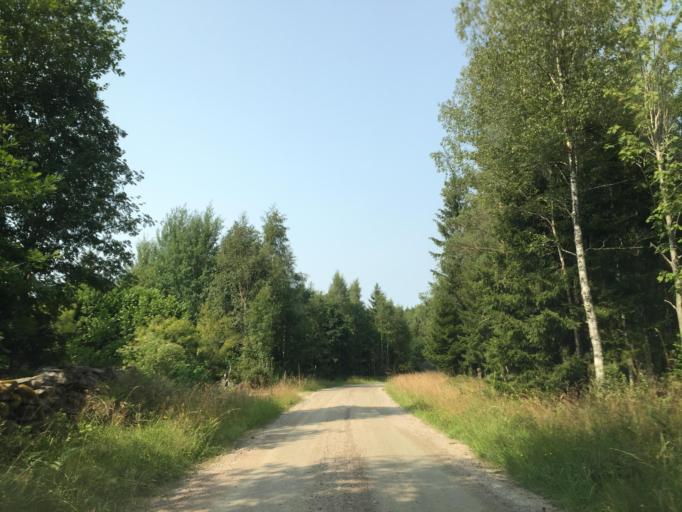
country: SE
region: Vaestra Goetaland
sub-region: Lilla Edets Kommun
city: Lilla Edet
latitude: 58.2554
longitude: 12.0934
